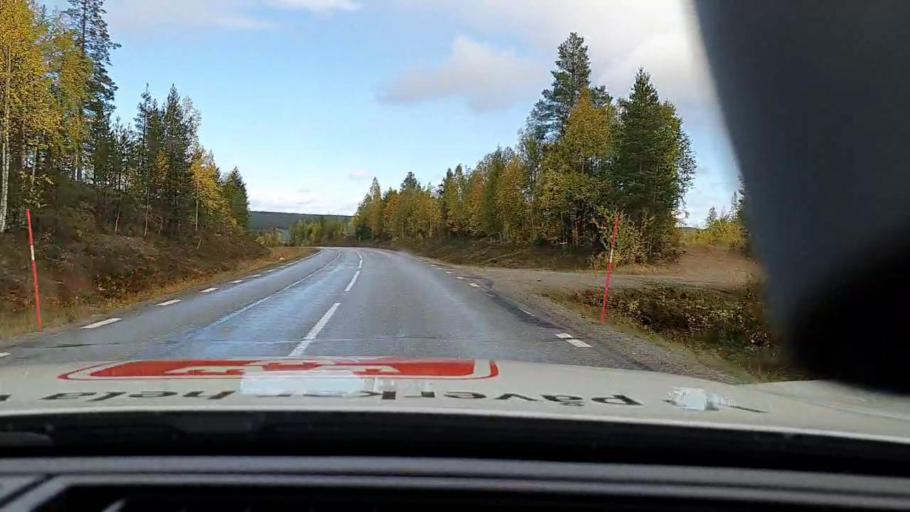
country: SE
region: Vaesterbotten
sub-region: Norsjo Kommun
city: Norsjoe
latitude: 64.9558
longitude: 19.6912
